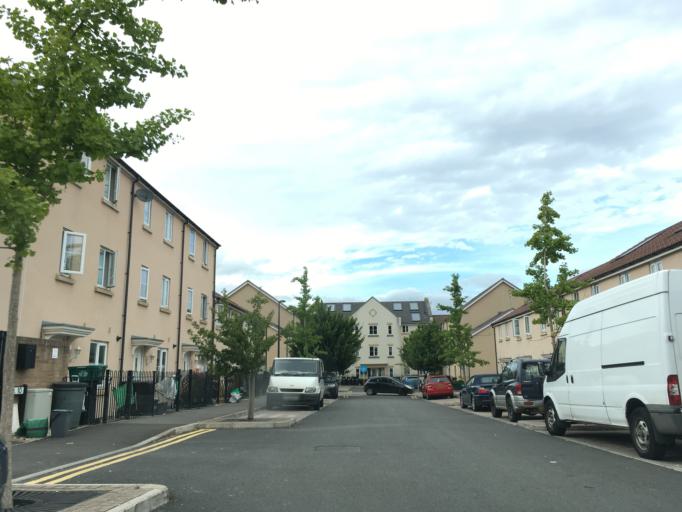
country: GB
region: England
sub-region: South Gloucestershire
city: Stoke Gifford
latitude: 51.4971
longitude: -2.5545
